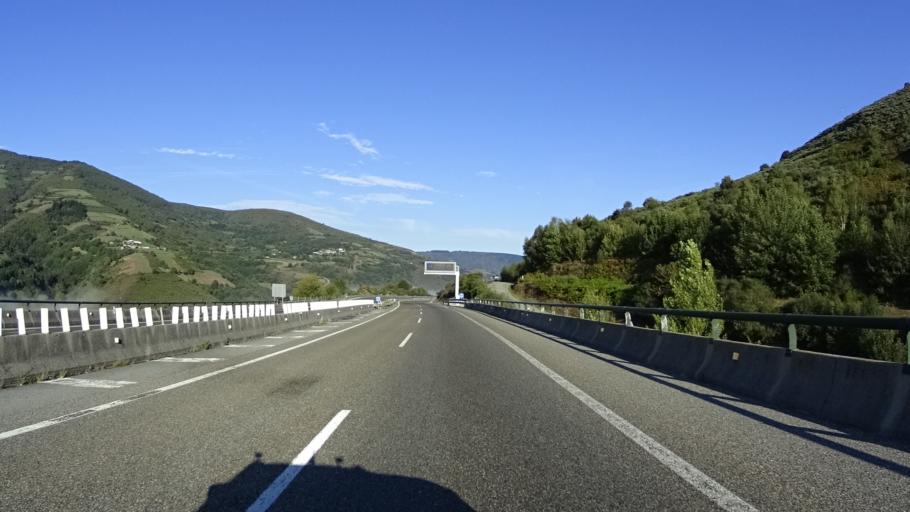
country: ES
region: Galicia
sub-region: Provincia de Lugo
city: San Roman
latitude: 42.7543
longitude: -7.0688
